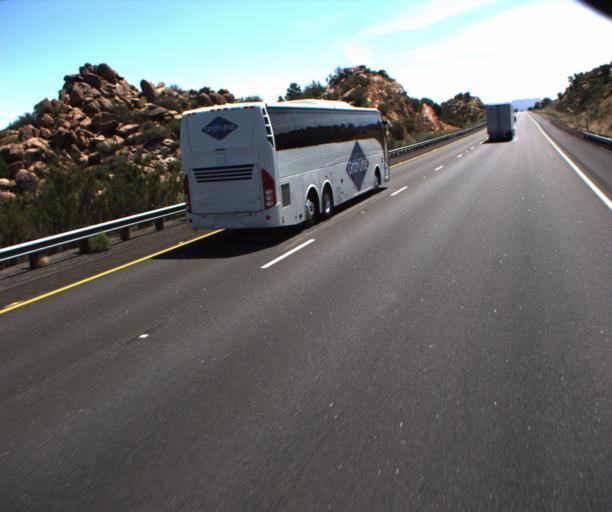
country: US
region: Arizona
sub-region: Mohave County
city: Peach Springs
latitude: 35.1845
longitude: -113.4003
